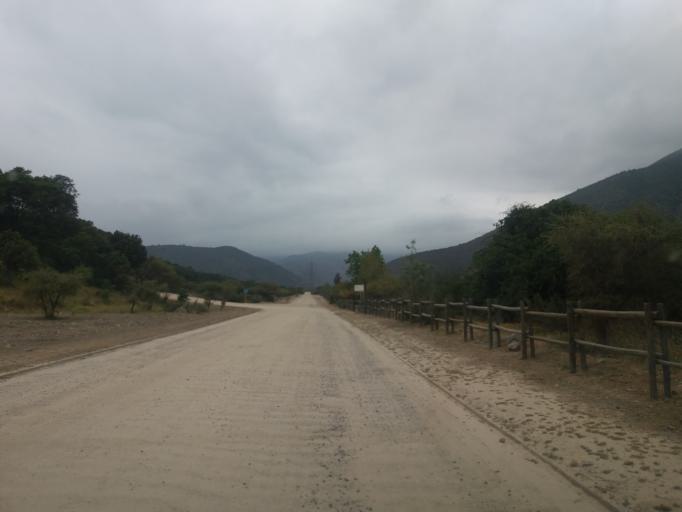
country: CL
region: Valparaiso
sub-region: Provincia de Marga Marga
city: Limache
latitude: -33.0281
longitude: -71.1378
